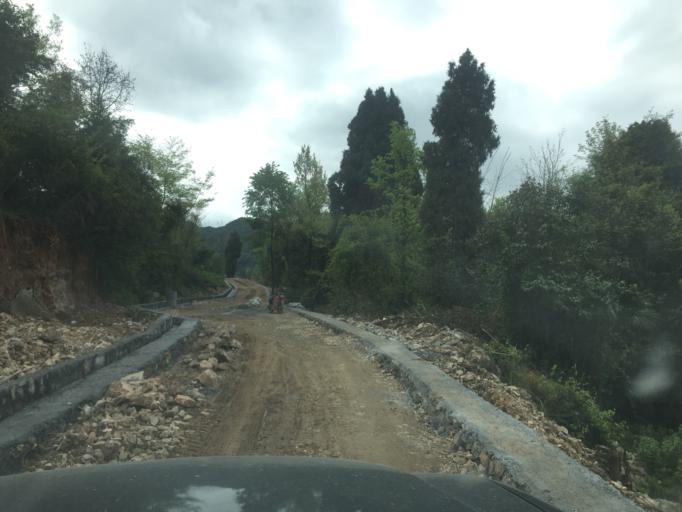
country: CN
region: Guizhou Sheng
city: Jiancha
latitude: 28.1878
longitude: 107.9882
